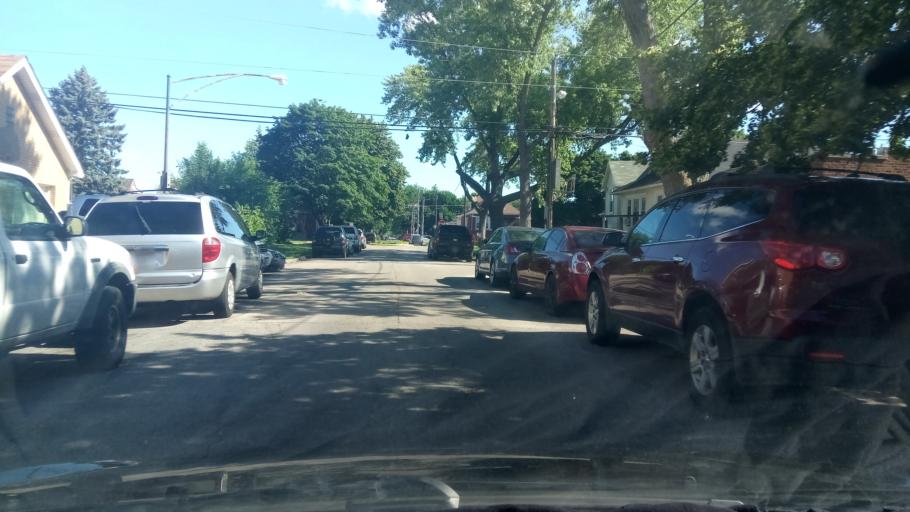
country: US
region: Illinois
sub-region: Cook County
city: Hometown
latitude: 41.7807
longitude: -87.7180
